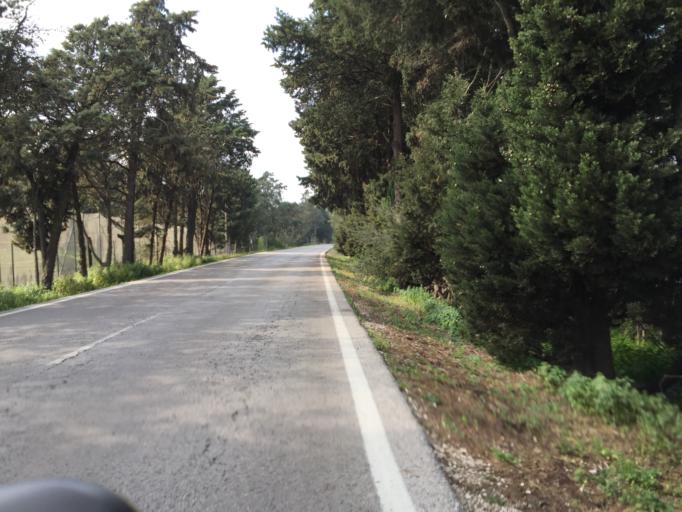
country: ES
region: Andalusia
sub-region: Provincia de Cadiz
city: Benalup-Casas Viejas
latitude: 36.3073
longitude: -5.8958
